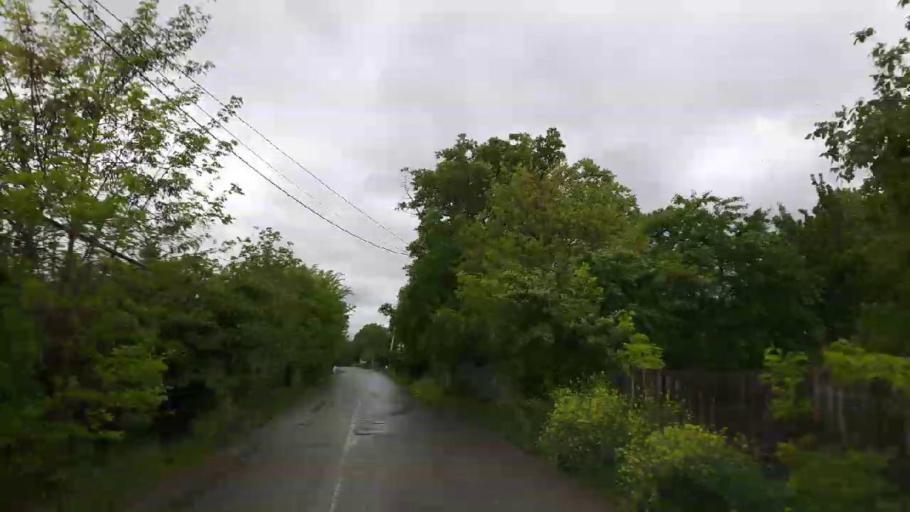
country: GE
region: Shida Kartli
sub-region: Khashuris Raioni
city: Khashuri
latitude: 41.9828
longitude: 43.6749
